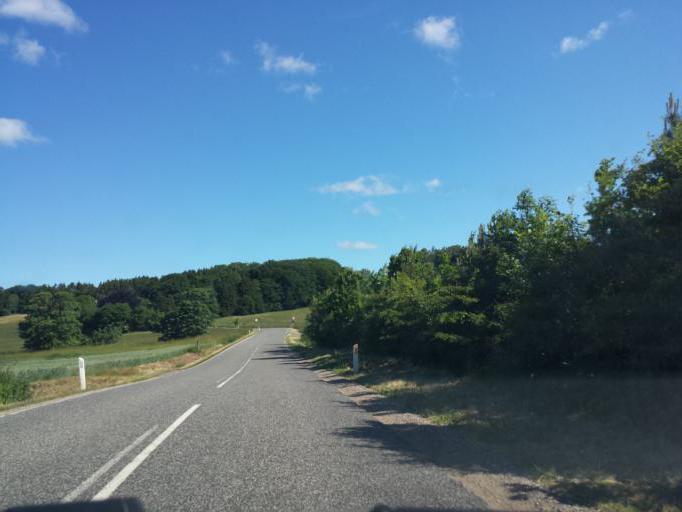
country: DK
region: Capital Region
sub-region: Egedal Kommune
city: Ganlose
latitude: 55.8021
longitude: 12.2644
